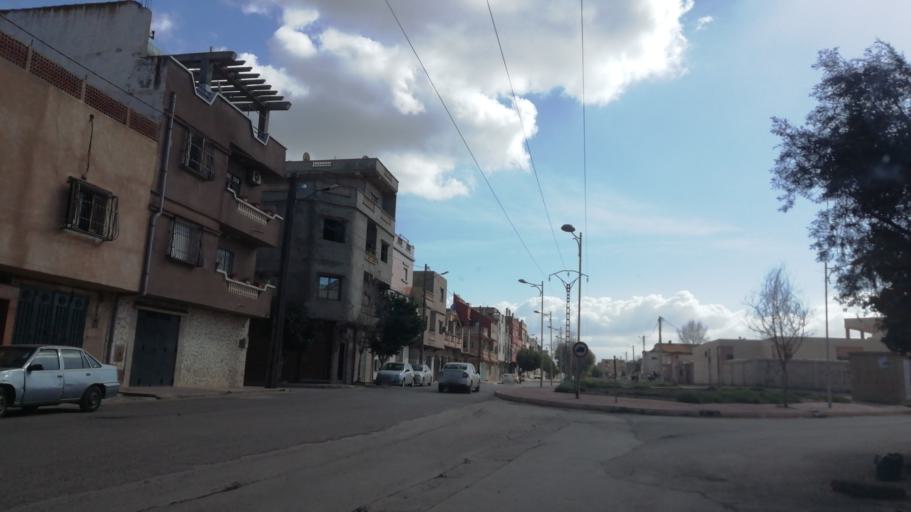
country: DZ
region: Oran
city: Es Senia
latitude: 35.6220
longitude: -0.5833
